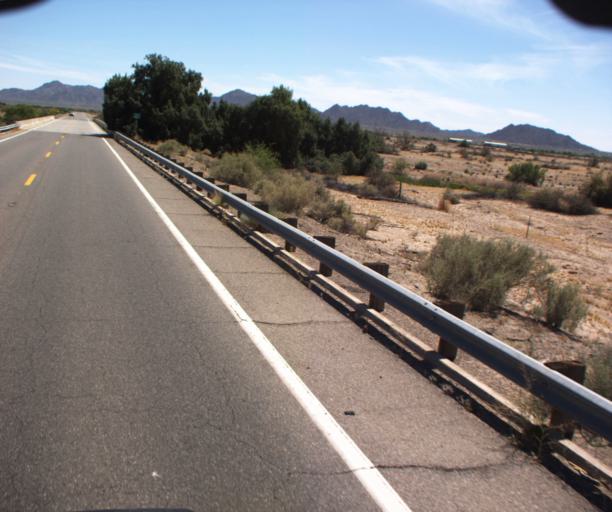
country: US
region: Arizona
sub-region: Pinal County
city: Sacaton
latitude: 33.0912
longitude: -111.7086
